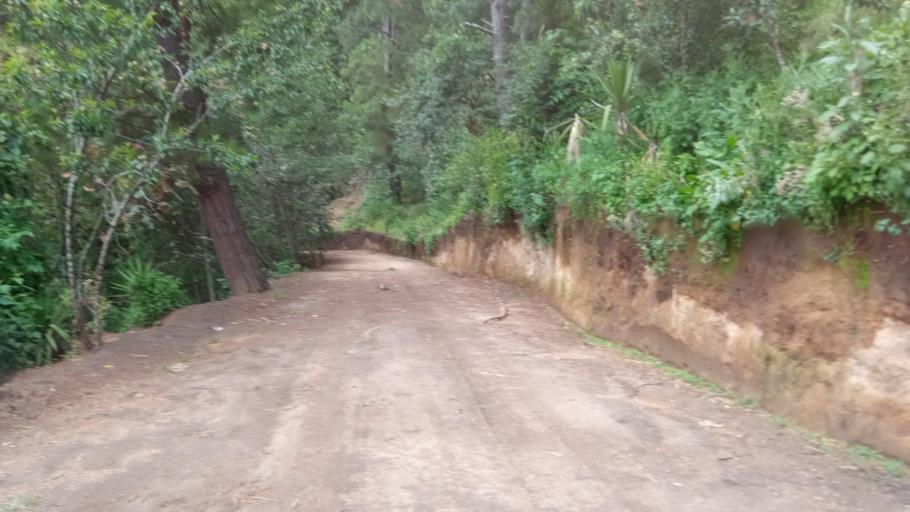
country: GT
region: San Marcos
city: Tejutla
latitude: 15.1157
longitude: -91.8047
